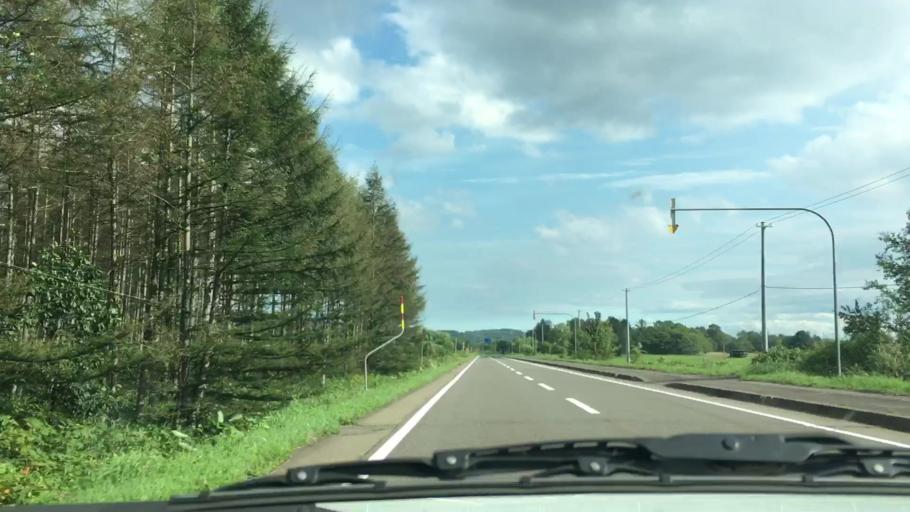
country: JP
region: Hokkaido
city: Otofuke
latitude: 43.3273
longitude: 143.2970
